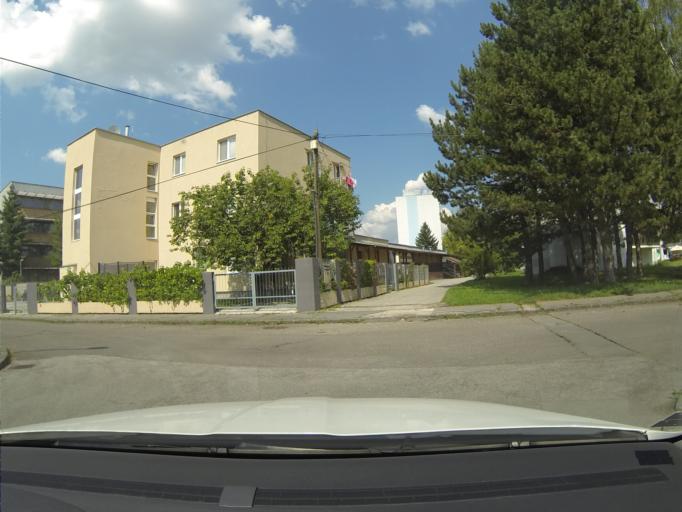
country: SK
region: Nitriansky
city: Prievidza
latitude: 48.7782
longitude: 18.6140
